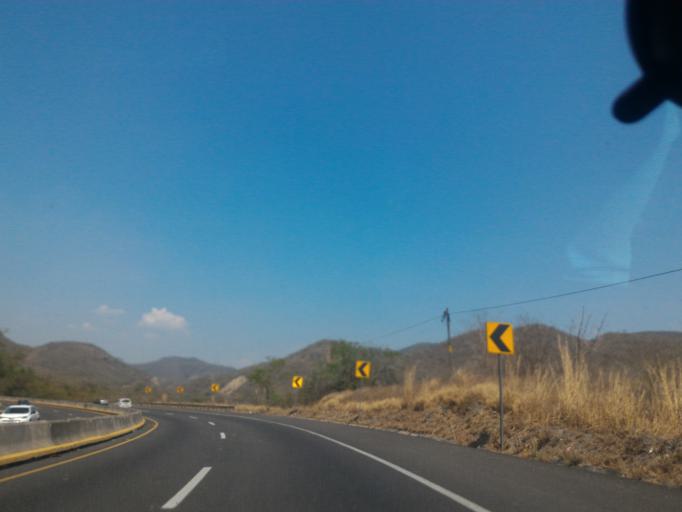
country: MX
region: Colima
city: Ixtlahuacan
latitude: 19.0390
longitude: -103.7899
